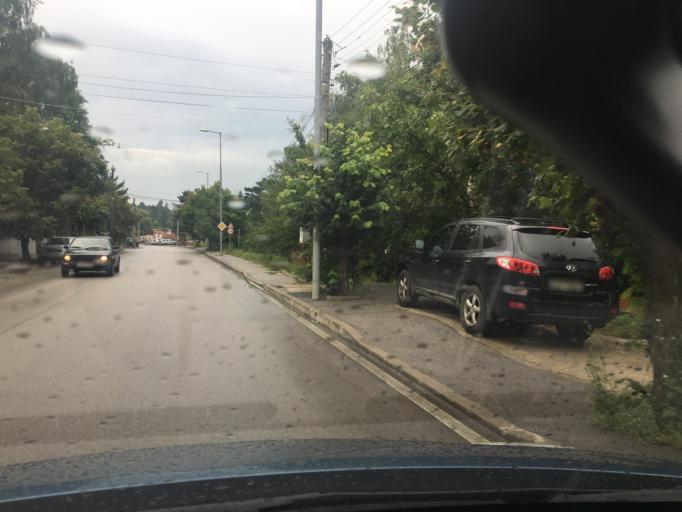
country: BG
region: Sofia-Capital
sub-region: Stolichna Obshtina
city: Sofia
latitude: 42.6348
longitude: 23.3031
